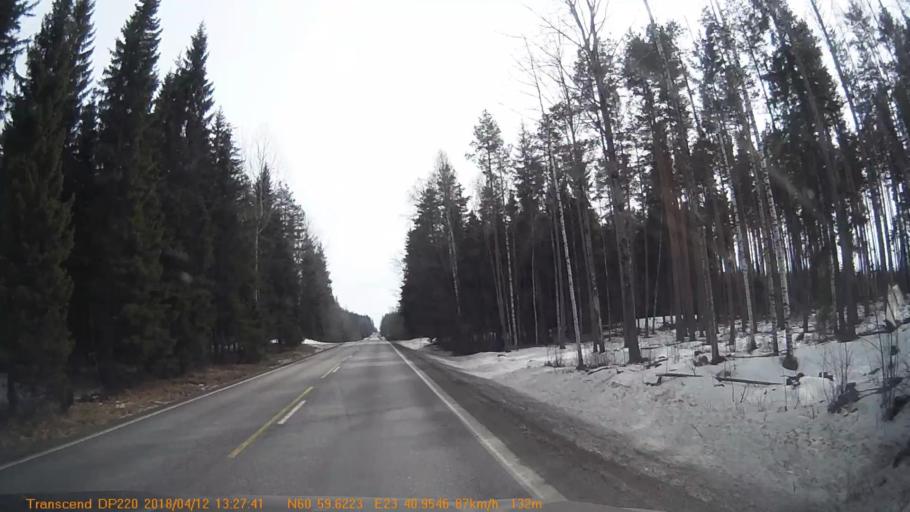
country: FI
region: Pirkanmaa
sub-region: Etelae-Pirkanmaa
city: Kylmaekoski
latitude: 60.9935
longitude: 23.6827
